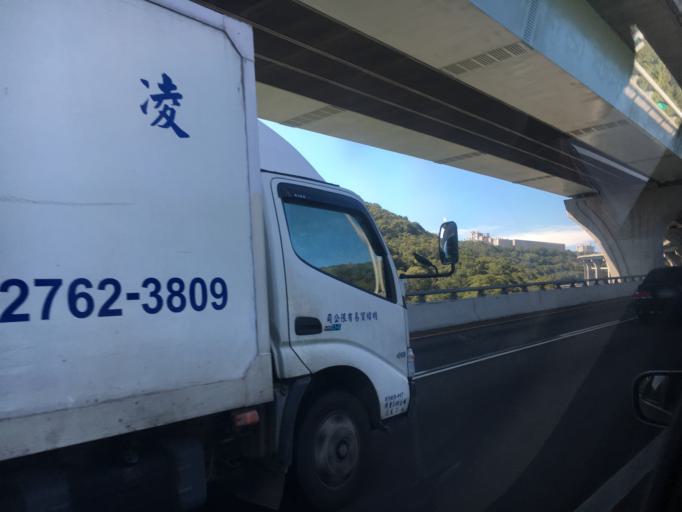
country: TW
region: Taipei
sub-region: Taipei
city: Banqiao
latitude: 25.0650
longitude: 121.3905
